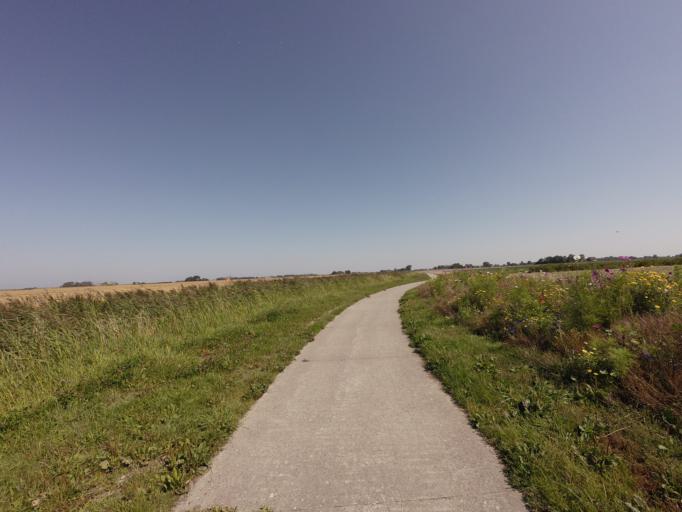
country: NL
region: Friesland
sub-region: Gemeente Dongeradeel
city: Anjum
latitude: 53.3843
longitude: 6.0571
